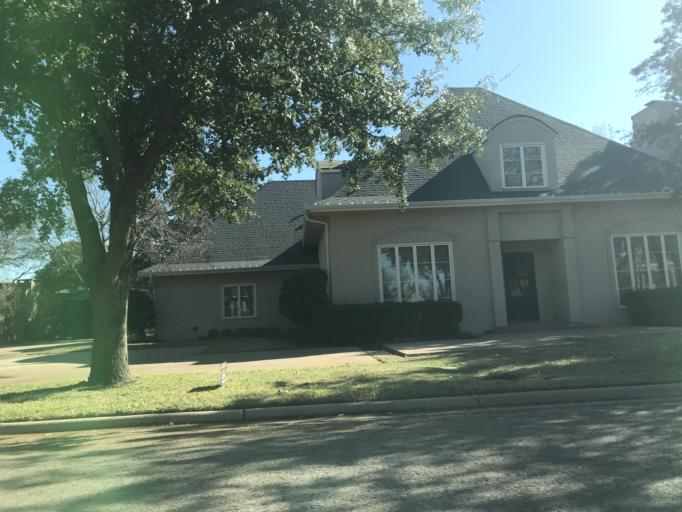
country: US
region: Texas
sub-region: Taylor County
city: Abilene
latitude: 32.3791
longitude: -99.7600
